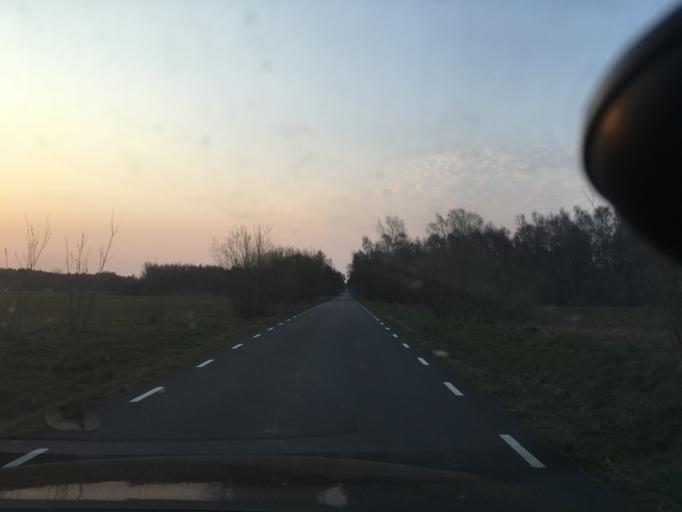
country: SE
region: Skane
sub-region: Simrishamns Kommun
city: Simrishamn
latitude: 55.3984
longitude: 14.1695
